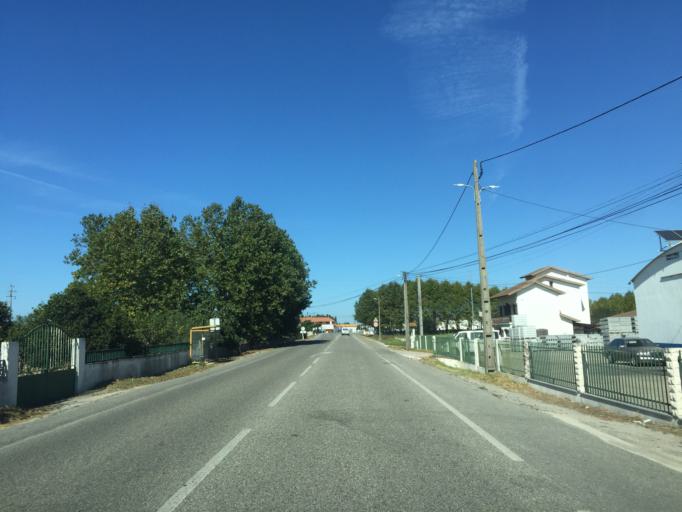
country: PT
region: Coimbra
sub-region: Figueira da Foz
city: Alhadas
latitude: 40.2638
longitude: -8.7796
